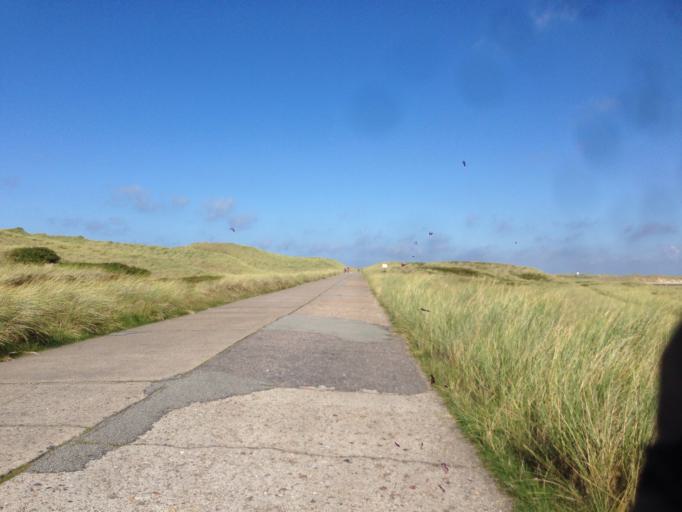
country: DE
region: Schleswig-Holstein
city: List
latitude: 55.0412
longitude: 8.3911
